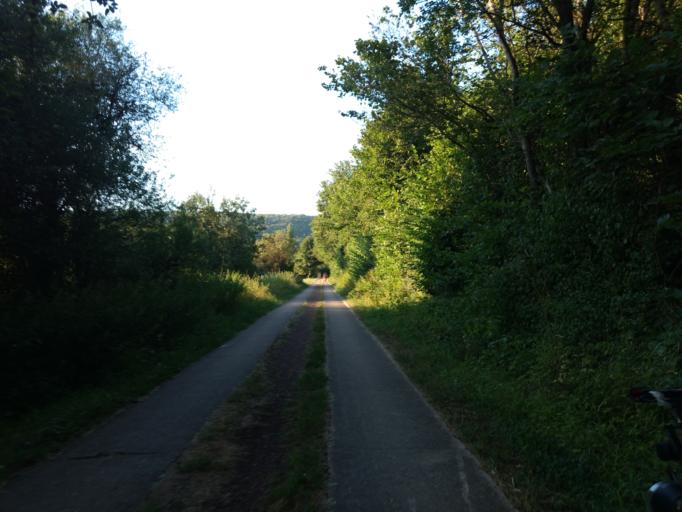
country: DE
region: Saarland
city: Rehlingen-Siersburg
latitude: 49.3592
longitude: 6.6297
